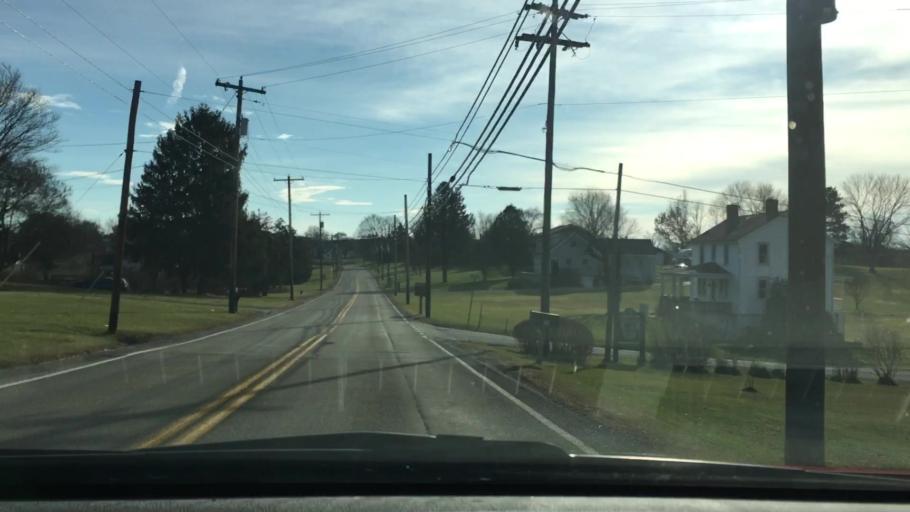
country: US
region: Pennsylvania
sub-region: Westmoreland County
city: West Newton
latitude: 40.1994
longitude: -79.7439
